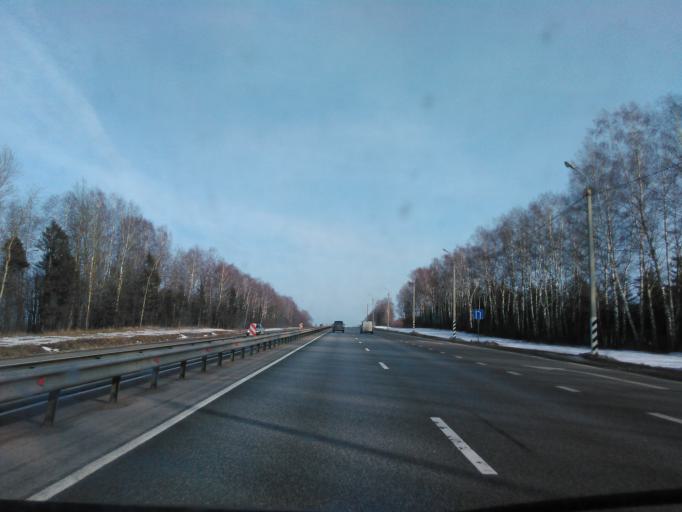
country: RU
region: Smolensk
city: Verkhnedneprovskiy
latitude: 55.1826
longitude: 33.5219
